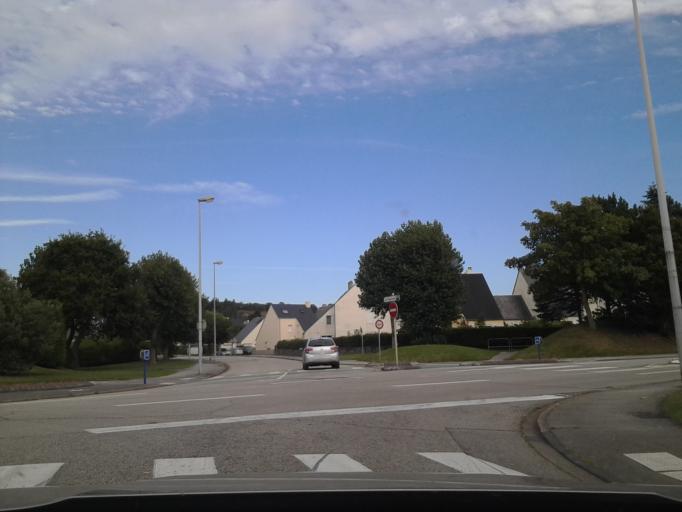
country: FR
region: Lower Normandy
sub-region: Departement de la Manche
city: Tourlaville
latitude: 49.6436
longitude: -1.5753
